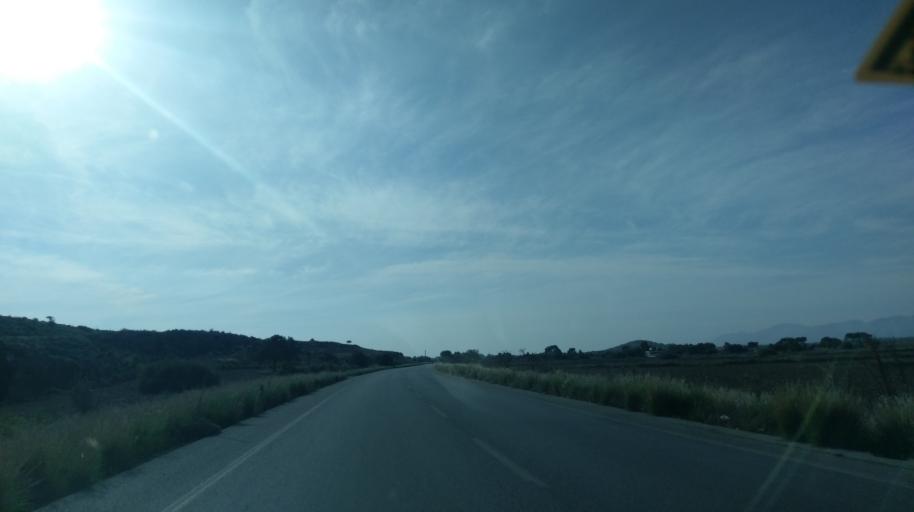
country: CY
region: Ammochostos
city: Lefkonoiko
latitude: 35.2688
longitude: 33.8106
